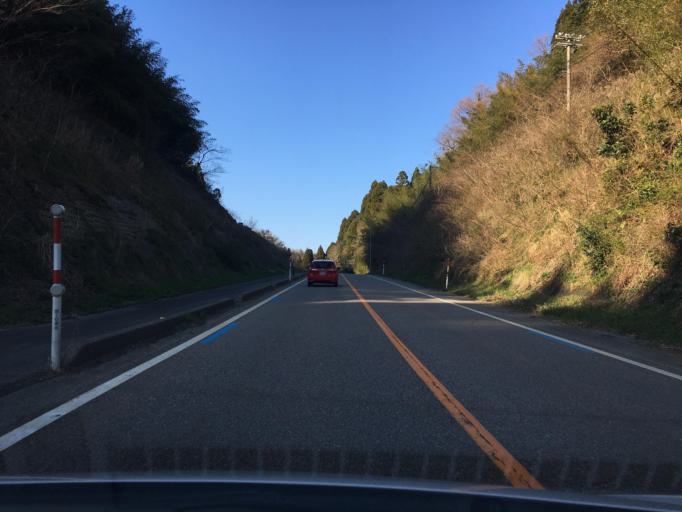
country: JP
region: Toyama
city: Himi
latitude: 36.9245
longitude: 137.0252
